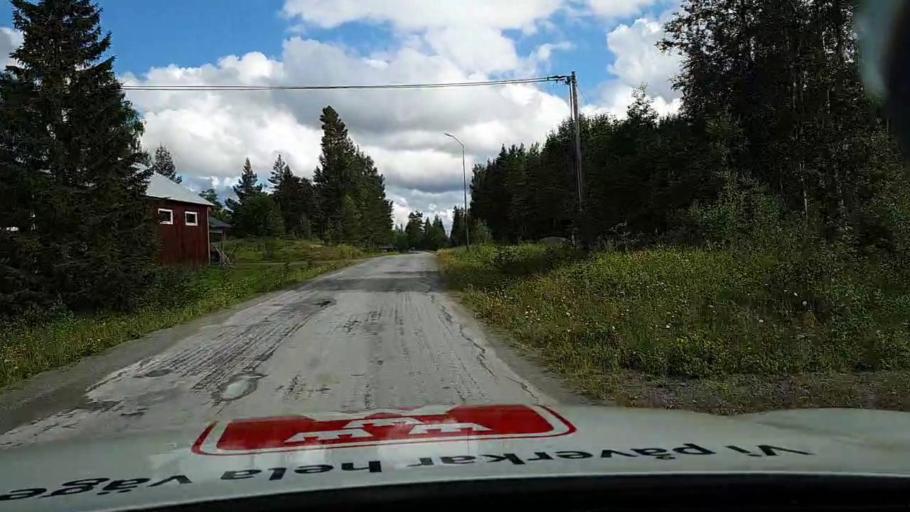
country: SE
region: Jaemtland
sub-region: OEstersunds Kommun
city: Brunflo
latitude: 63.1305
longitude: 15.0768
